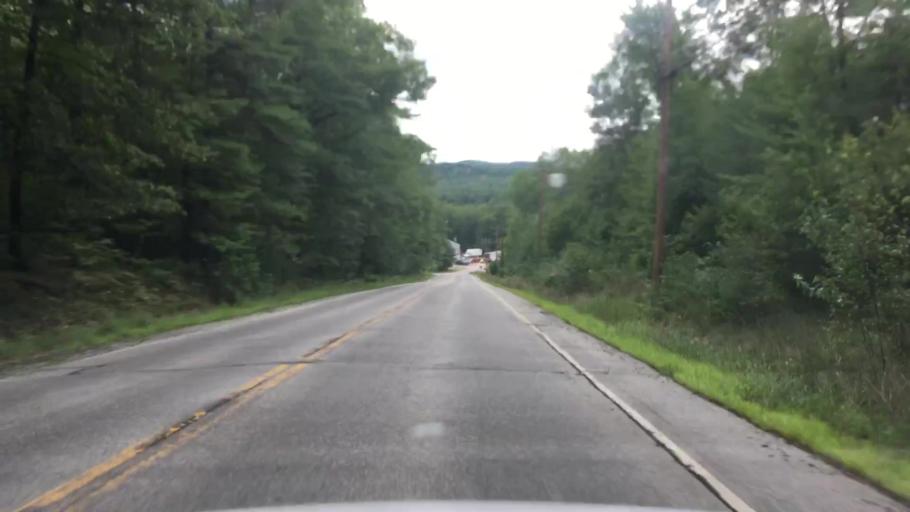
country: US
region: Maine
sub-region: York County
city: Cornish
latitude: 43.8110
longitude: -70.7777
